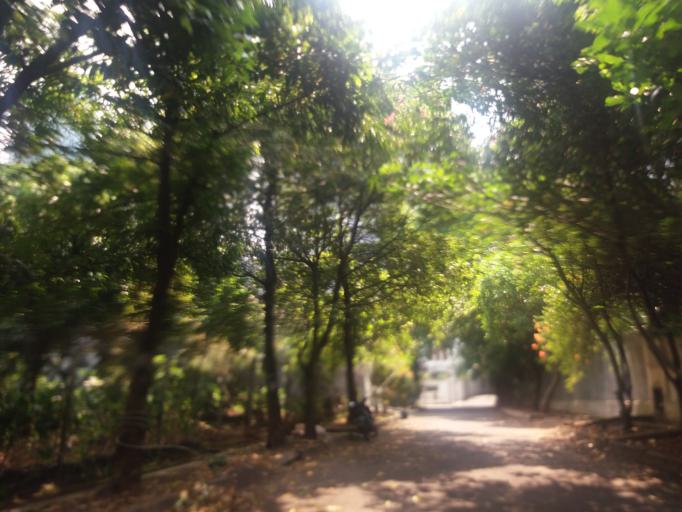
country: ID
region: Jakarta Raya
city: Jakarta
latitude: -6.2270
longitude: 106.8312
